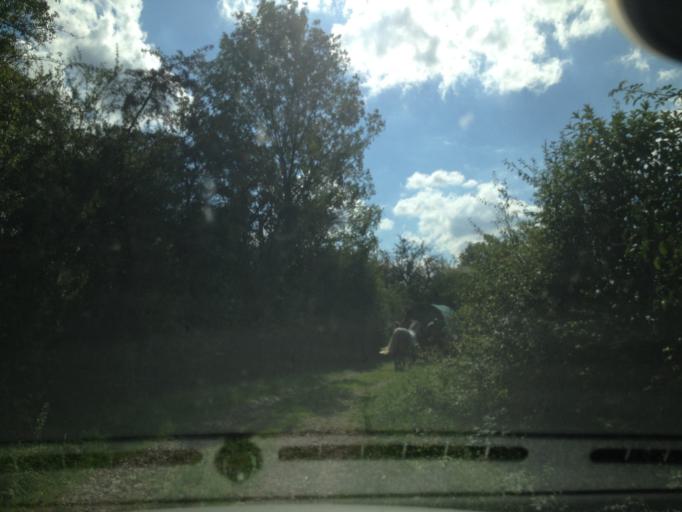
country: FR
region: Franche-Comte
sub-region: Departement de la Haute-Saone
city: Saint-Loup-sur-Semouse
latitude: 47.8253
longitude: 6.2086
